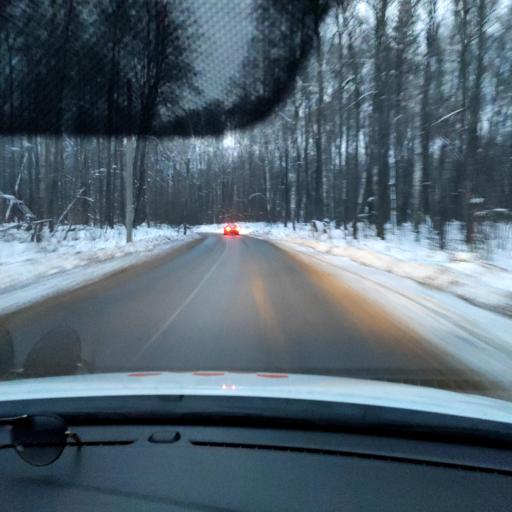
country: RU
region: Tatarstan
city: Vysokaya Gora
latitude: 55.9278
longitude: 49.1946
